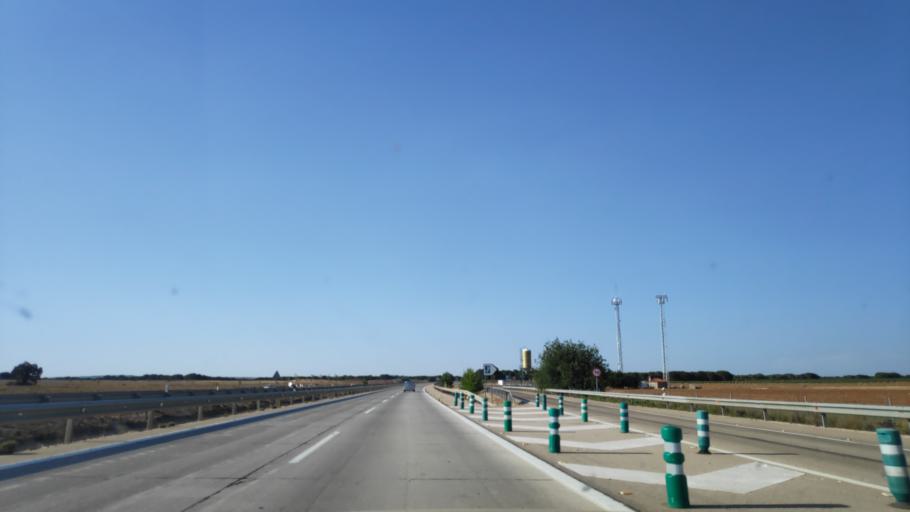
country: ES
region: Castille-La Mancha
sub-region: Provincia de Cuenca
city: Pozoamargo
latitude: 39.3201
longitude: -2.2033
